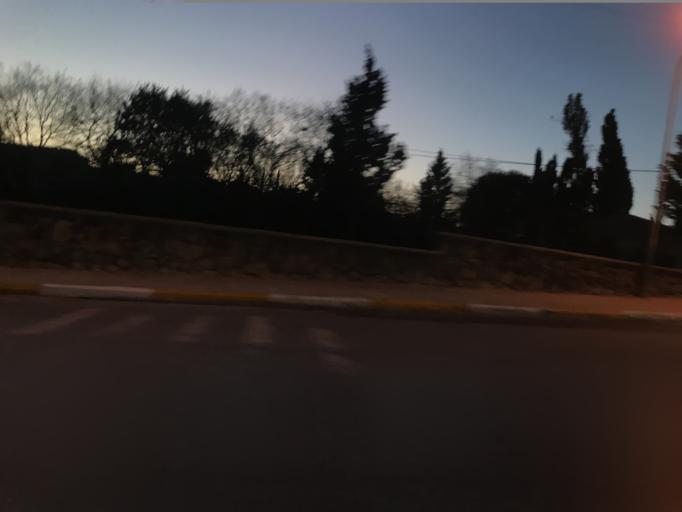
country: TR
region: Istanbul
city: Pendik
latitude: 40.9011
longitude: 29.2724
